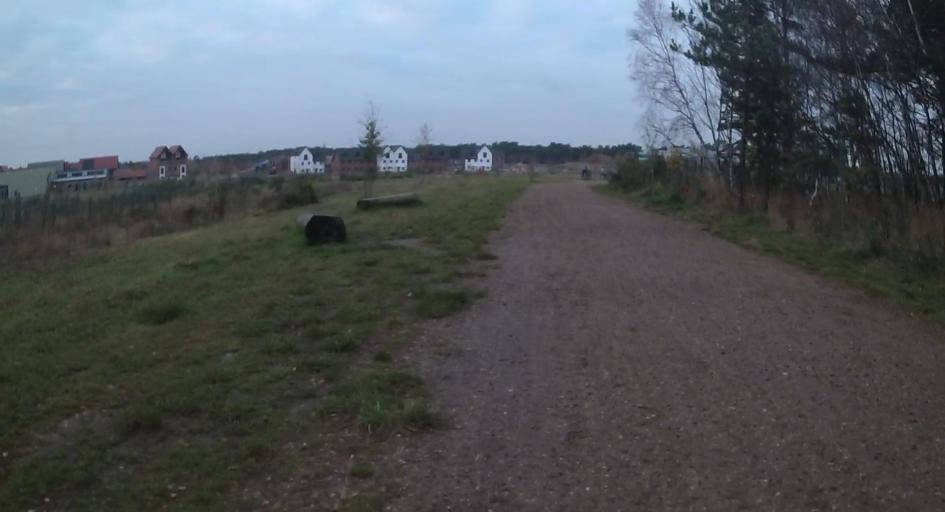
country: GB
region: England
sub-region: Bracknell Forest
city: Crowthorne
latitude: 51.3786
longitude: -0.7835
